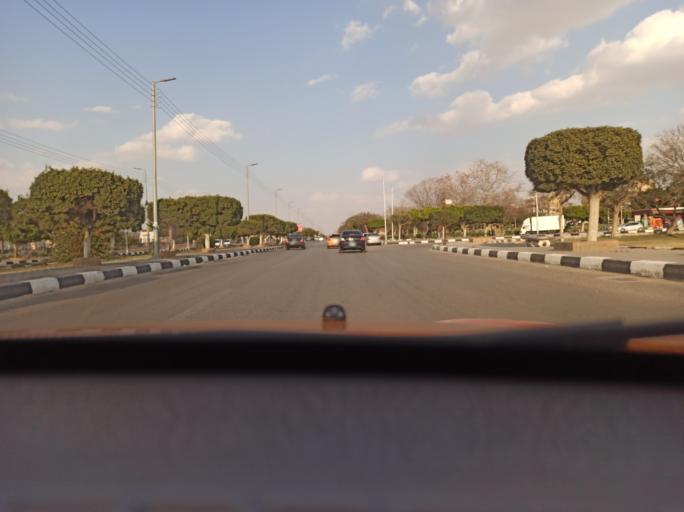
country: EG
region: Al Isma'iliyah
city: Ismailia
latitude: 30.6189
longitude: 32.2738
